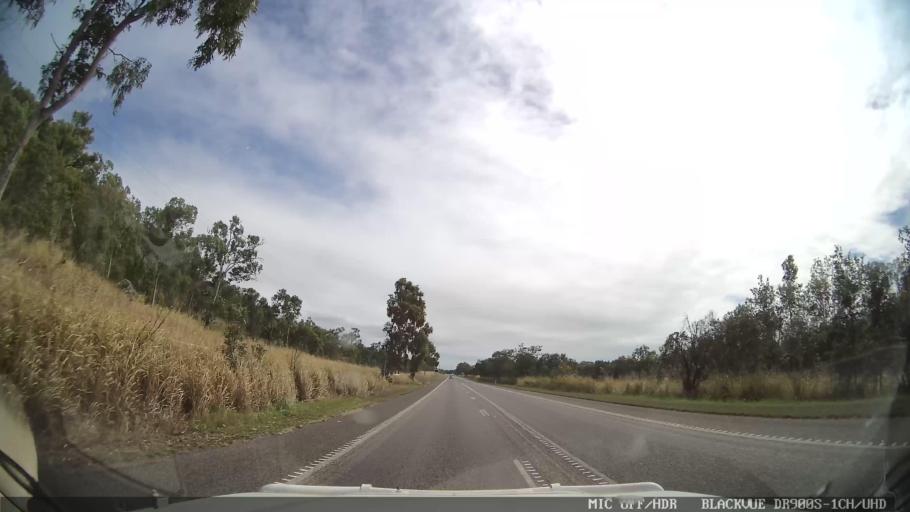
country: AU
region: Queensland
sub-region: Hinchinbrook
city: Ingham
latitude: -19.0076
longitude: 146.3614
